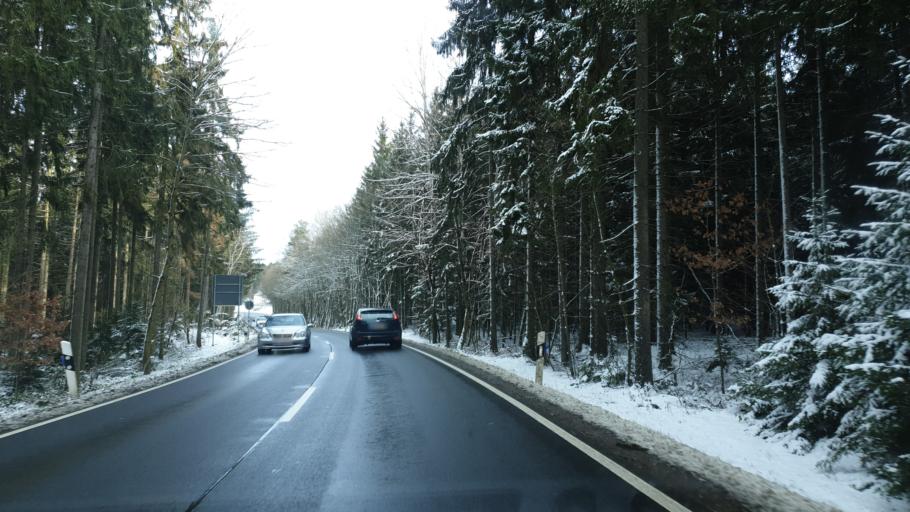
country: DE
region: Saxony
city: Triebel
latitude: 50.3810
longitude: 12.1497
